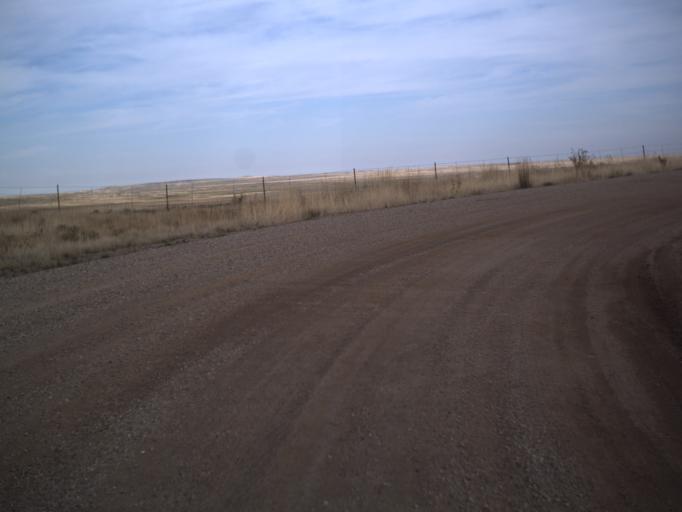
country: US
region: Utah
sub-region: Millard County
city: Fillmore
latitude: 38.7660
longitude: -112.5567
